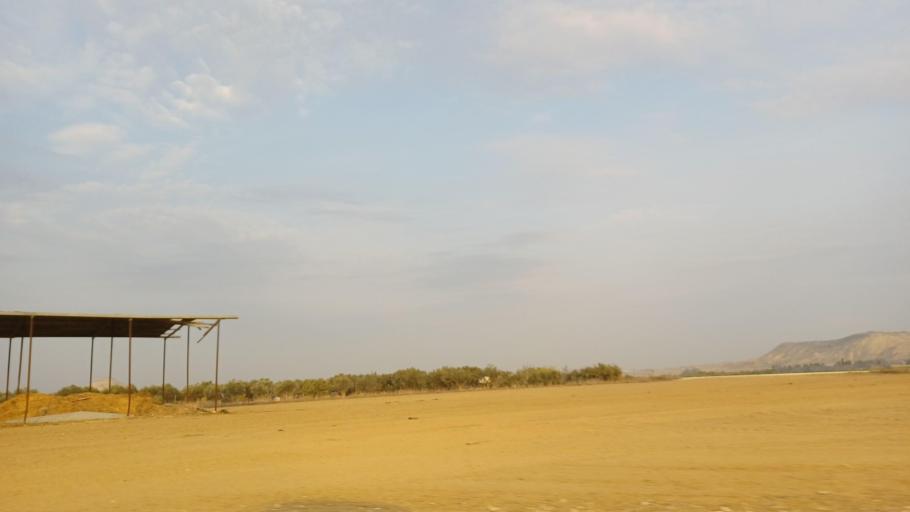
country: CY
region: Larnaka
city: Athienou
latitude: 35.0571
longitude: 33.5148
